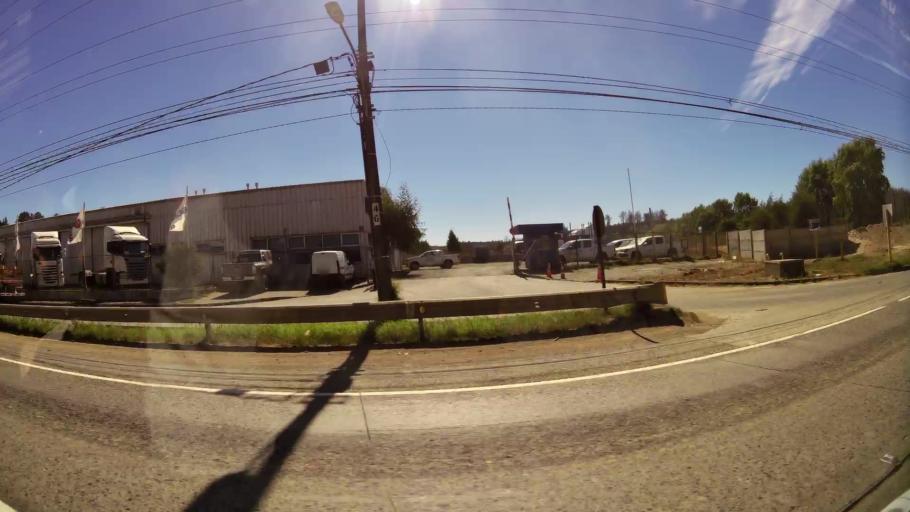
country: CL
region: Biobio
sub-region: Provincia de Concepcion
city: Penco
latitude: -36.7711
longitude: -73.0144
